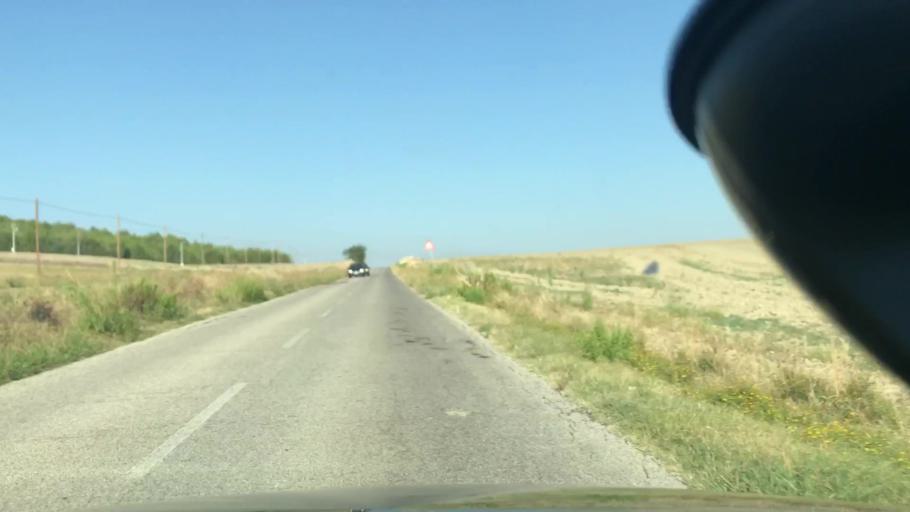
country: IT
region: Basilicate
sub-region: Provincia di Matera
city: La Martella
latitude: 40.6646
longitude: 16.4964
